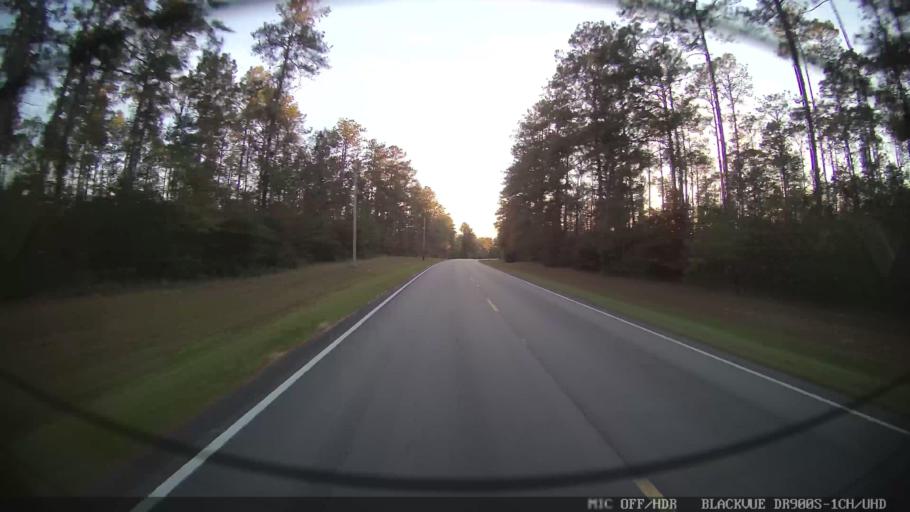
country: US
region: Mississippi
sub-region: Stone County
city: Wiggins
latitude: 31.0376
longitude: -89.2159
